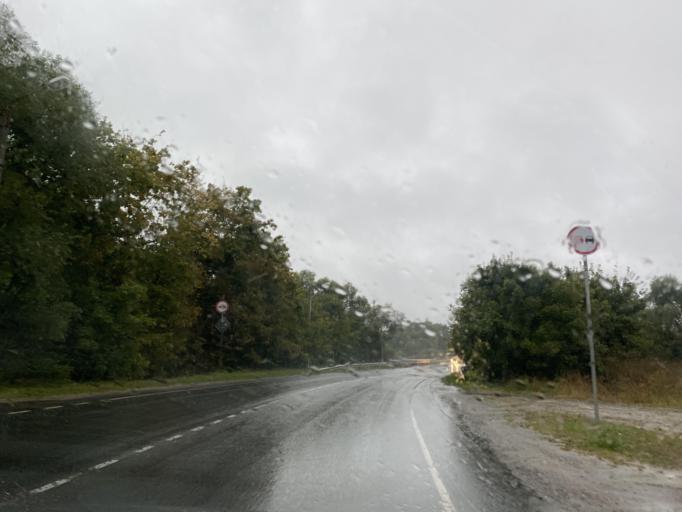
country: RU
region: Rjazan
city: Starozhilovo
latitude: 54.3794
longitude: 39.9256
